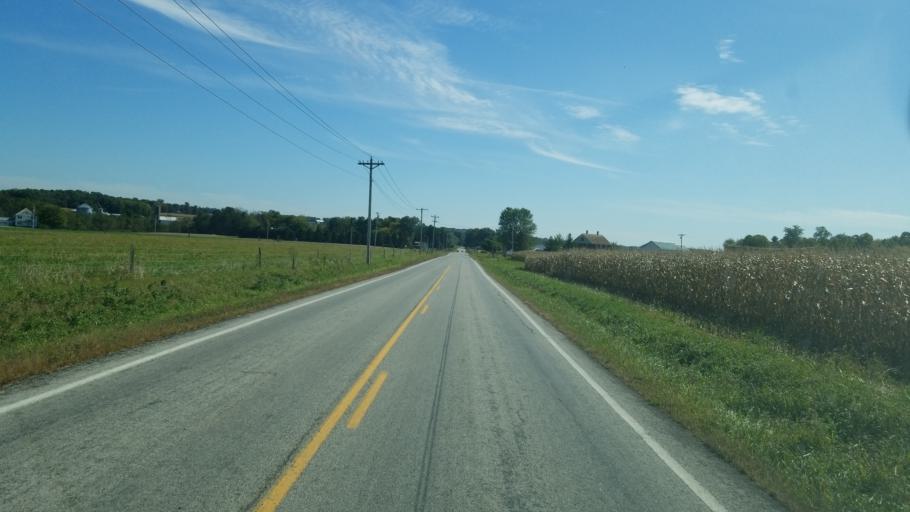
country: US
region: Ohio
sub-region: Wayne County
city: West Salem
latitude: 40.8607
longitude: -82.0759
